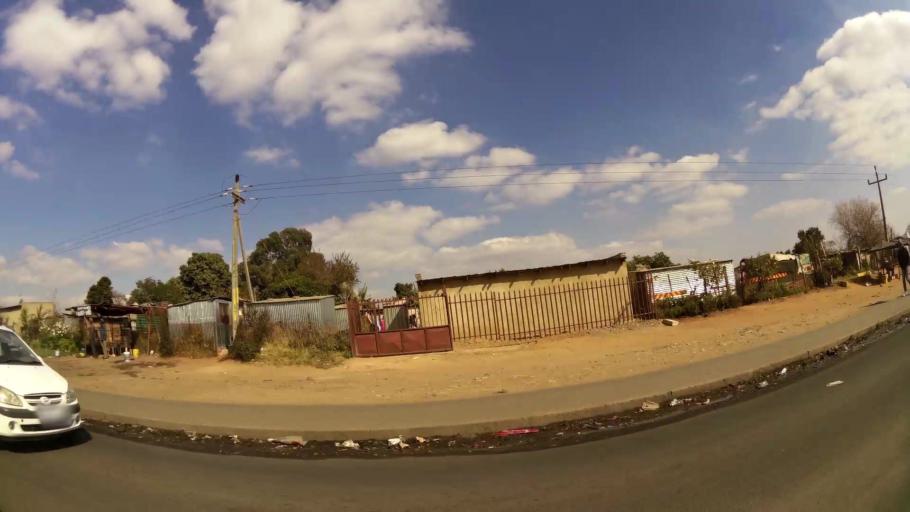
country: ZA
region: Gauteng
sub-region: Ekurhuleni Metropolitan Municipality
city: Tembisa
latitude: -25.9939
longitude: 28.2021
